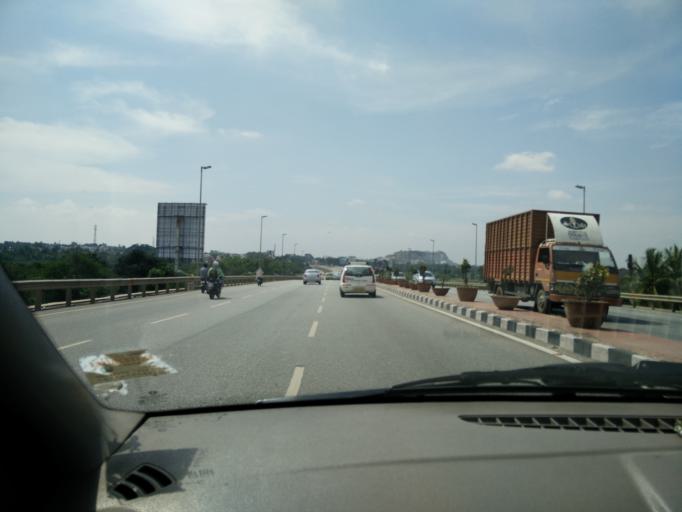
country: IN
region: Karnataka
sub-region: Bangalore Urban
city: Yelahanka
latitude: 13.1801
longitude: 77.6385
